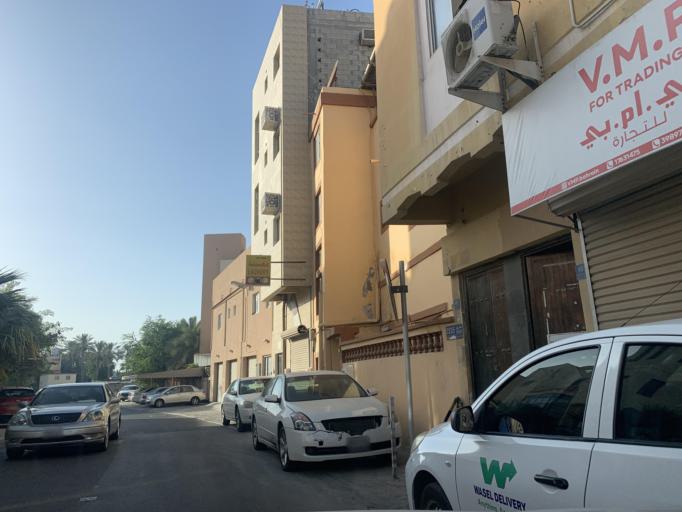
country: BH
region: Manama
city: Jidd Hafs
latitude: 26.2218
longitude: 50.5341
